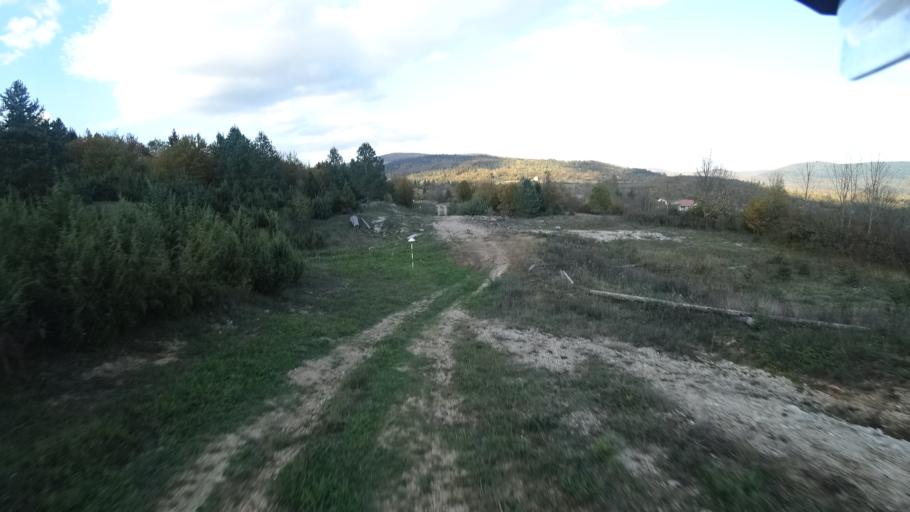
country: HR
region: Karlovacka
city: Plaski
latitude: 44.9958
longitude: 15.4227
